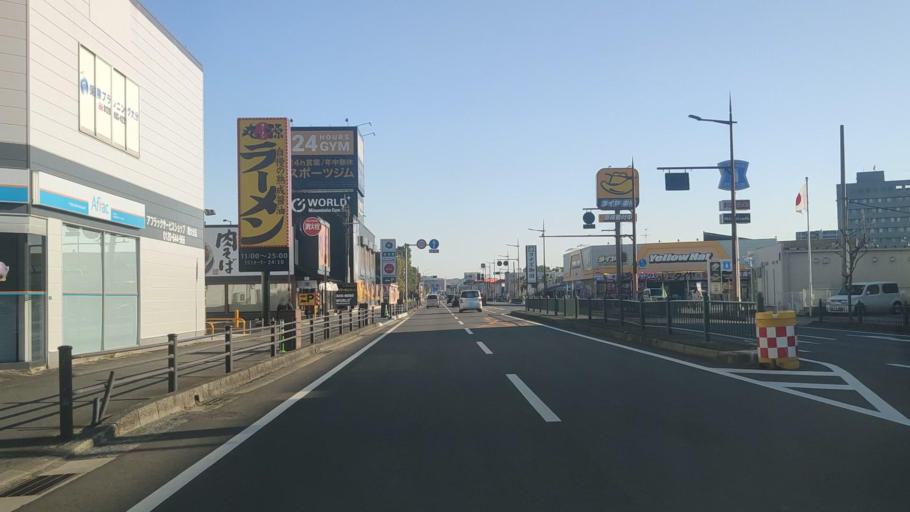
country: JP
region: Oita
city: Oita
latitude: 33.2103
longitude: 131.5988
